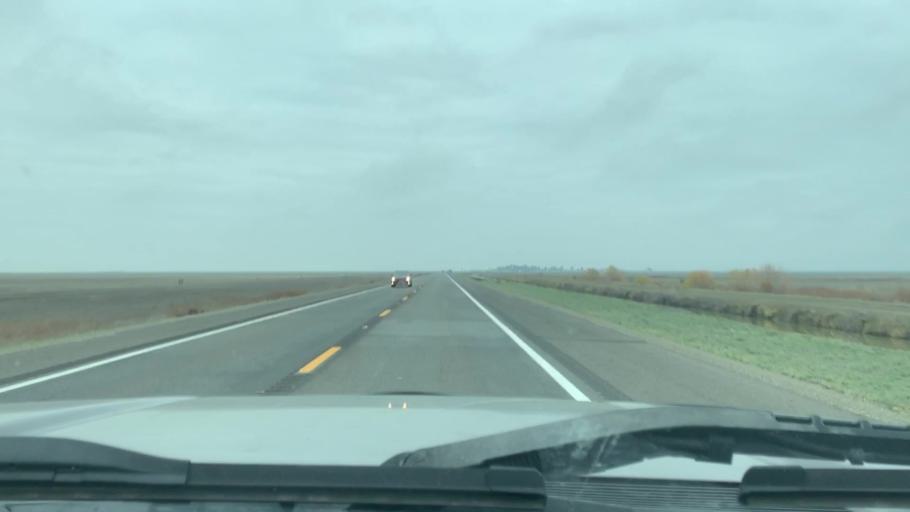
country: US
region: California
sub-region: Kings County
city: Kettleman City
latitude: 36.0976
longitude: -119.9083
